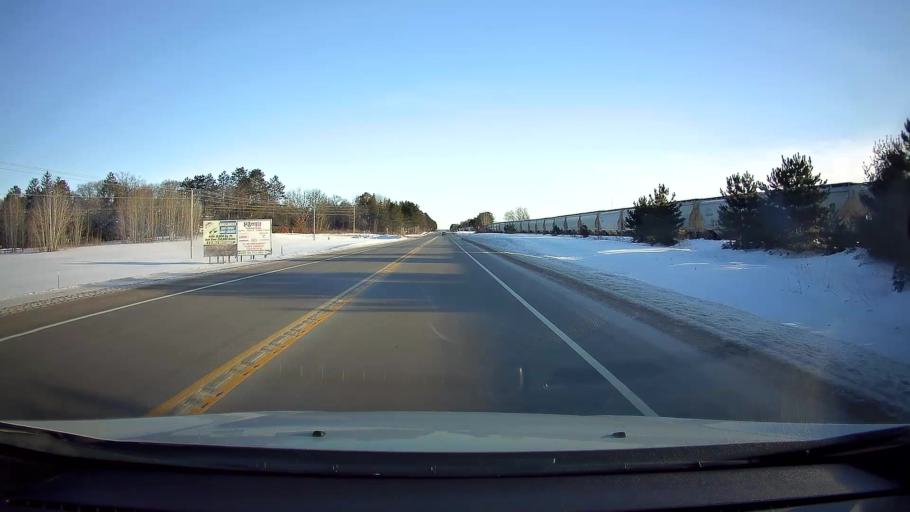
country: US
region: Wisconsin
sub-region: Washburn County
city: Spooner
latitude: 45.8420
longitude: -91.8769
